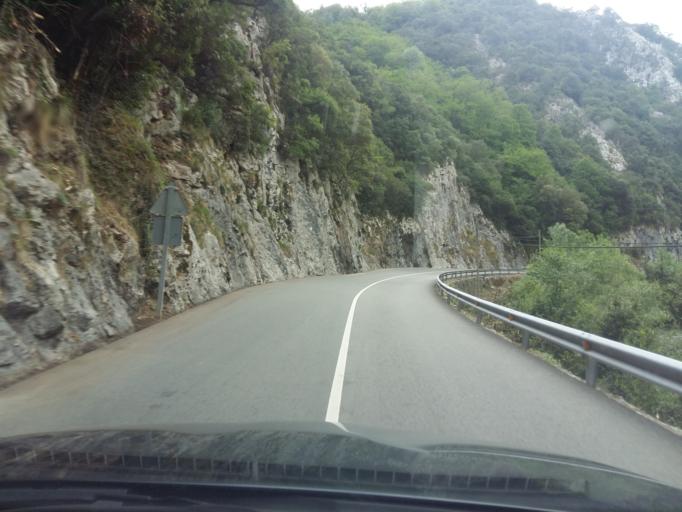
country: ES
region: Cantabria
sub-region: Provincia de Cantabria
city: Tresviso
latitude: 43.3099
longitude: -4.6086
